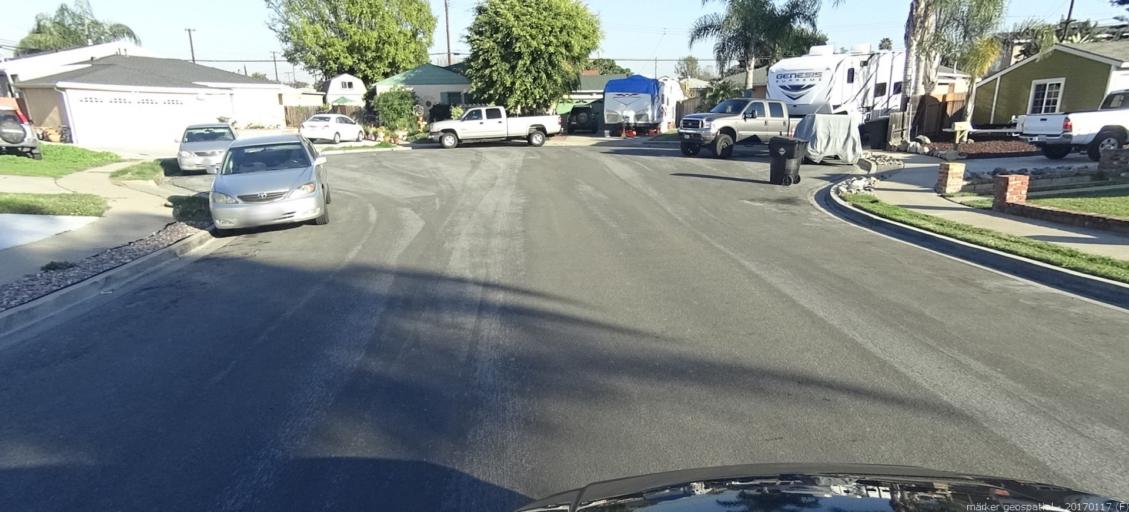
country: US
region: California
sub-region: Orange County
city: Midway City
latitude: 33.7399
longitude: -117.9927
